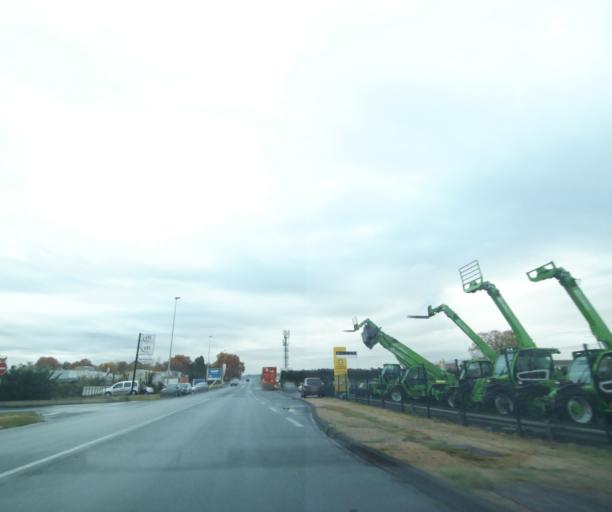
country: FR
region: Auvergne
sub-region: Departement du Puy-de-Dome
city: Aulnat
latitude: 45.7794
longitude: 3.1375
